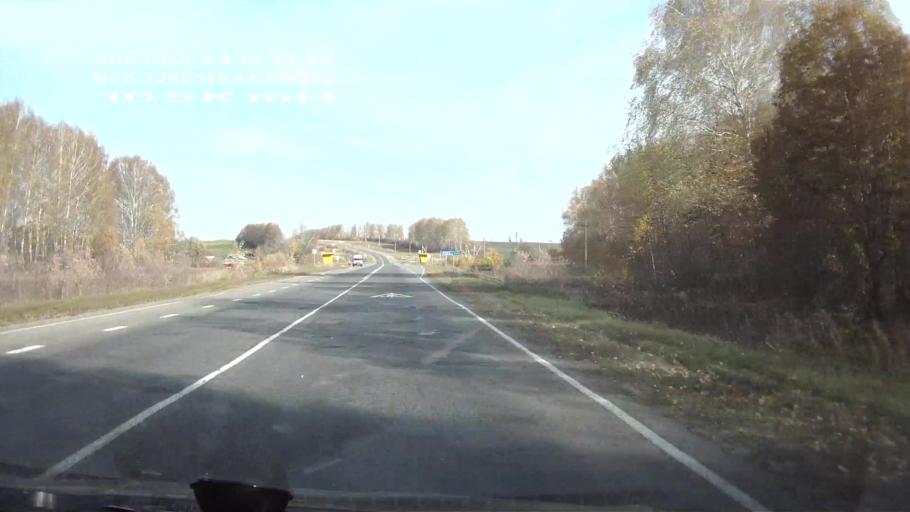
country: RU
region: Chuvashia
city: Ibresi
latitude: 55.3262
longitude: 47.1183
